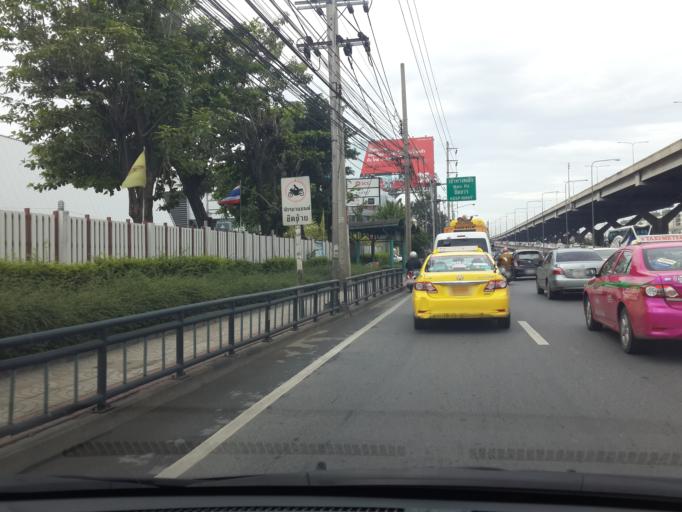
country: TH
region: Bangkok
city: Lak Si
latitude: 13.8952
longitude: 100.5881
